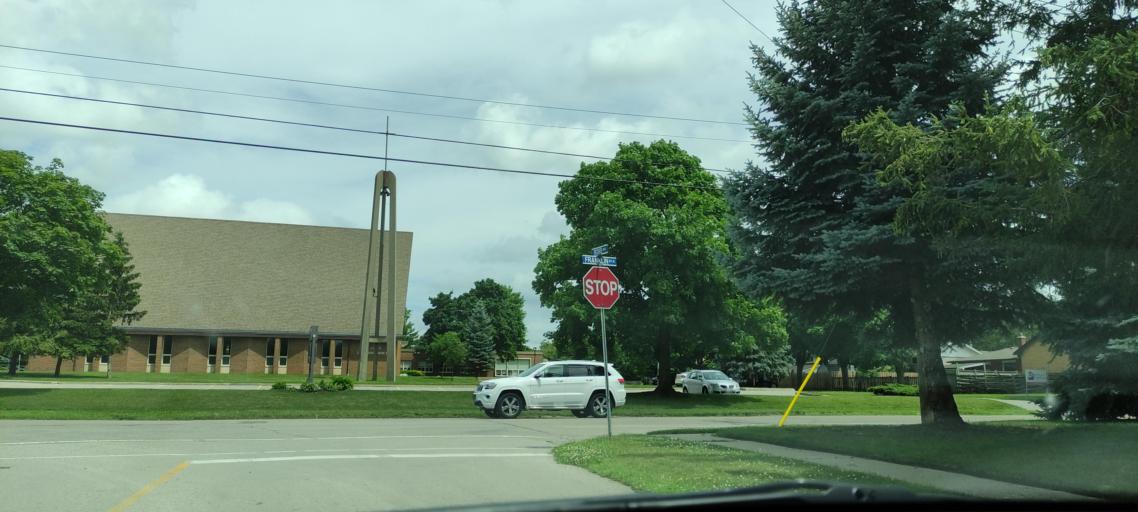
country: CA
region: Ontario
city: Kitchener
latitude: 43.4423
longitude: -80.4477
